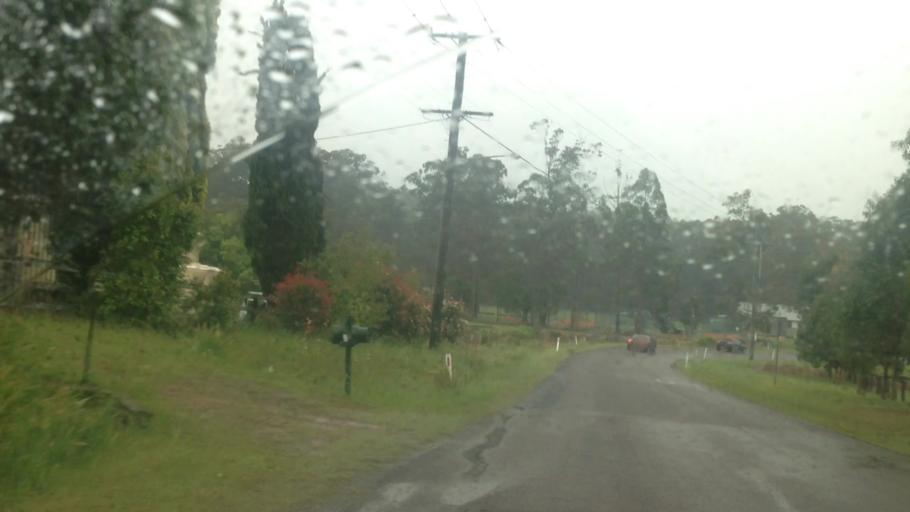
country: AU
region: New South Wales
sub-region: Wyong Shire
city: Little Jilliby
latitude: -33.1909
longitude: 151.3555
